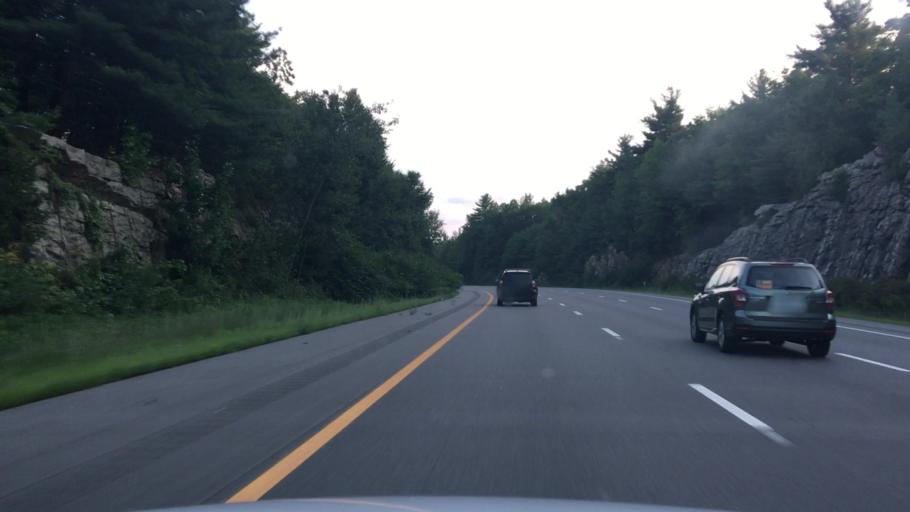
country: US
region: New Hampshire
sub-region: Merrimack County
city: Hooksett
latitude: 43.0557
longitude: -71.4739
